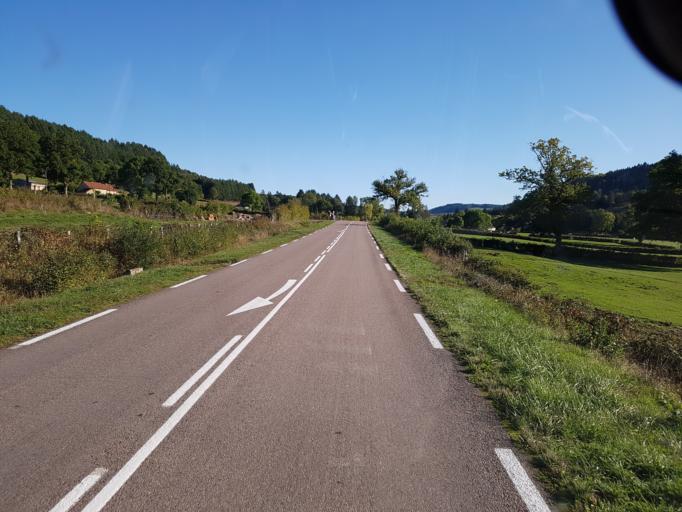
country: FR
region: Bourgogne
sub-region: Departement de Saone-et-Loire
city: Autun
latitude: 47.0922
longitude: 4.2378
